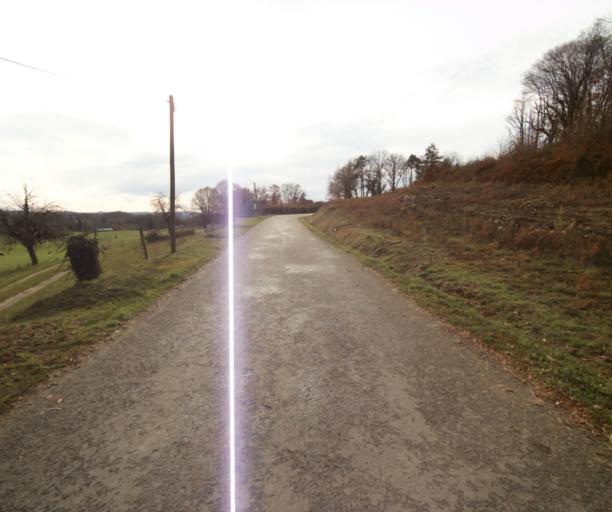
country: FR
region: Limousin
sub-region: Departement de la Correze
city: Chameyrat
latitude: 45.2578
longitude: 1.6877
